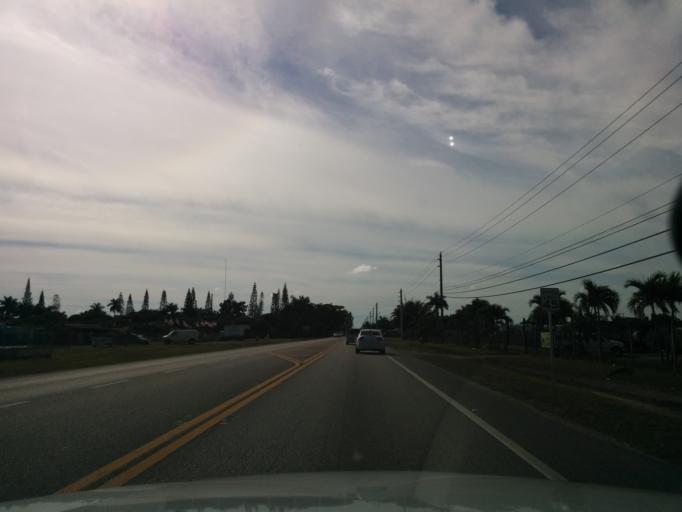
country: US
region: Florida
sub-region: Miami-Dade County
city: Richmond West
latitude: 25.5791
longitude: -80.4784
